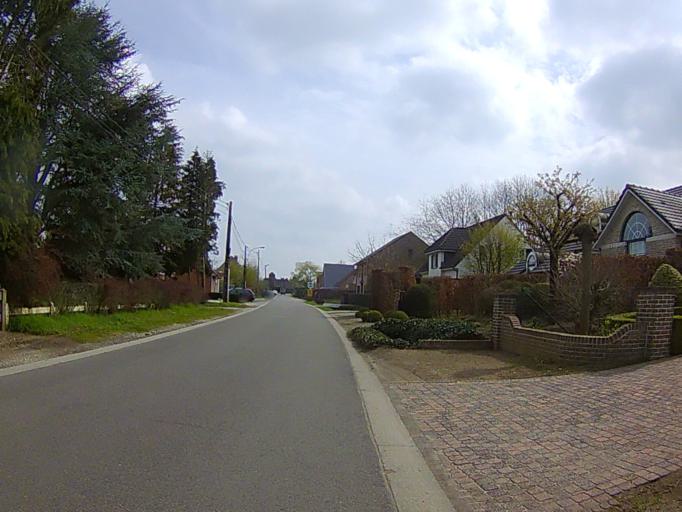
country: BE
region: Flanders
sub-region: Provincie Antwerpen
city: Grobbendonk
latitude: 51.1883
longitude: 4.7137
